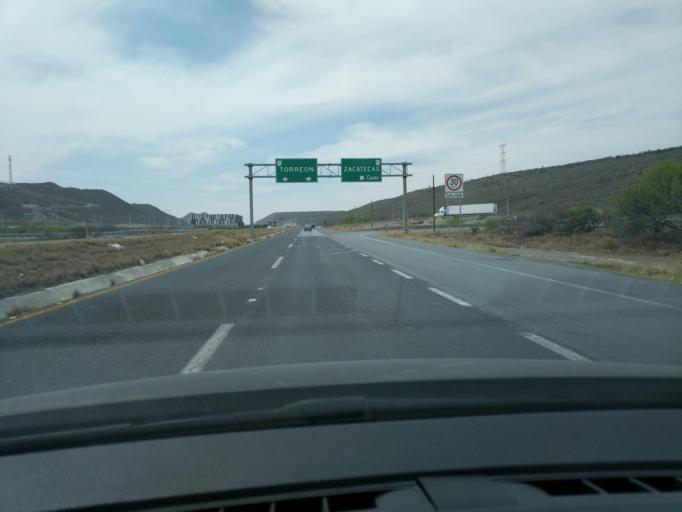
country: MX
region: Coahuila
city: Saltillo
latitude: 25.4536
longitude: -101.0664
